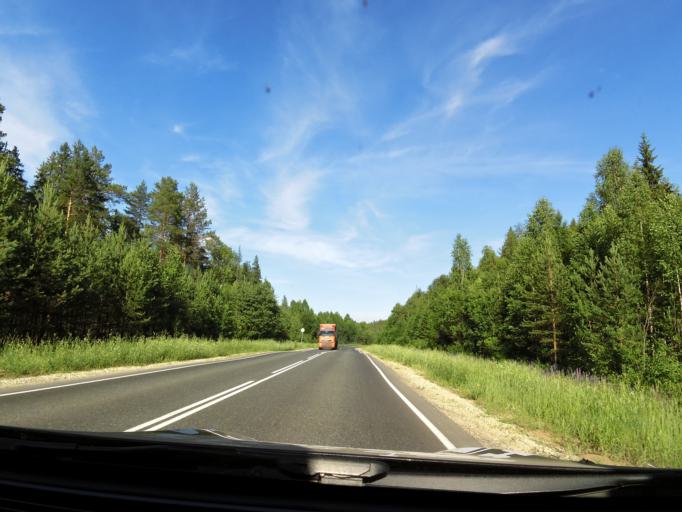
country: RU
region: Kirov
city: Dubrovka
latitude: 58.9079
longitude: 51.2434
